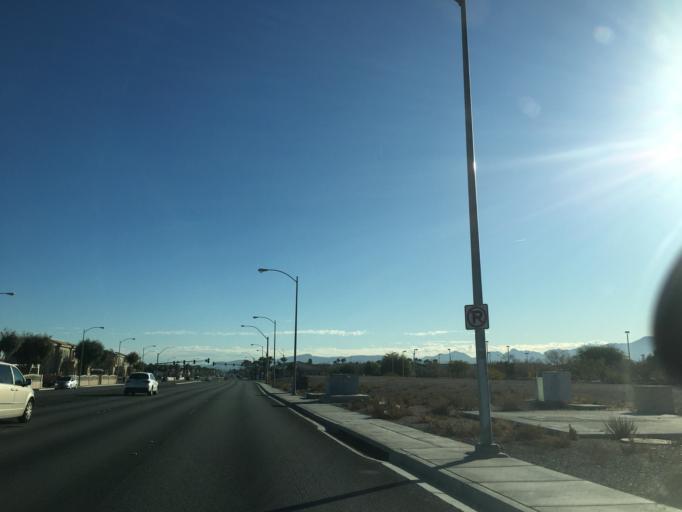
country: US
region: Nevada
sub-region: Clark County
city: Enterprise
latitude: 36.0135
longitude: -115.1661
